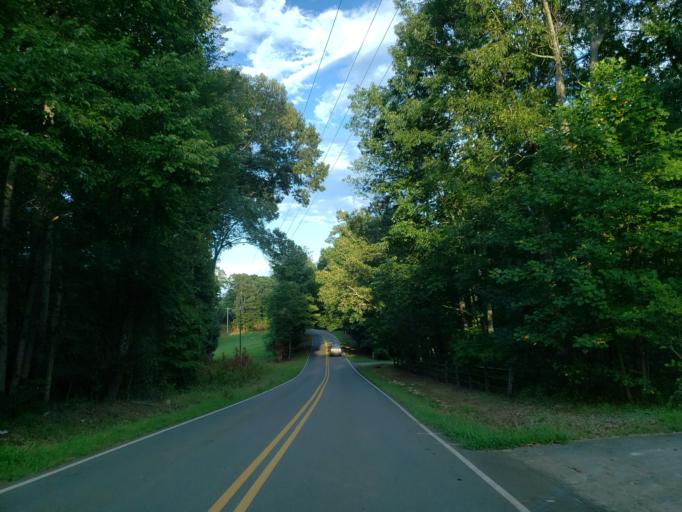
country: US
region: Georgia
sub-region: Cherokee County
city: Ball Ground
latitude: 34.3301
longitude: -84.4624
